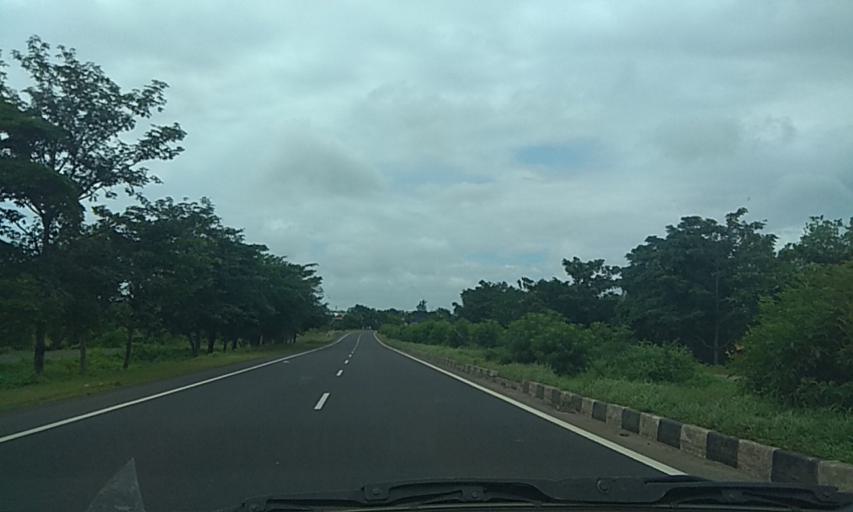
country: IN
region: Maharashtra
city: Nipani
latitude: 16.3812
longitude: 74.3909
